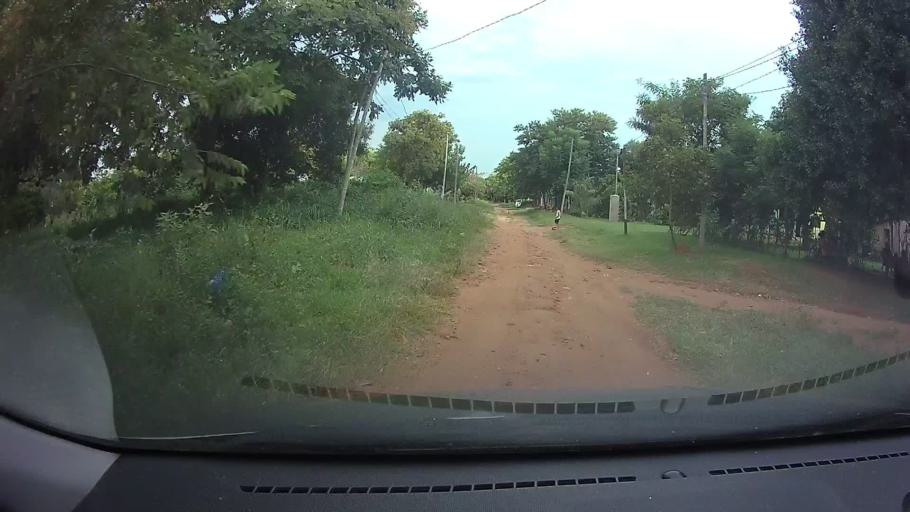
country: PY
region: Central
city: Limpio
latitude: -25.2443
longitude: -57.4518
